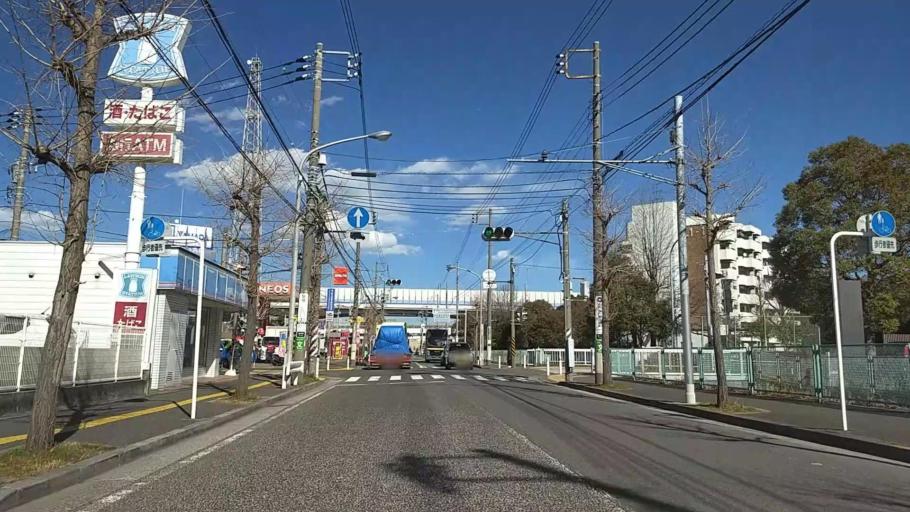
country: JP
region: Kanagawa
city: Yokohama
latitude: 35.3762
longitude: 139.6397
